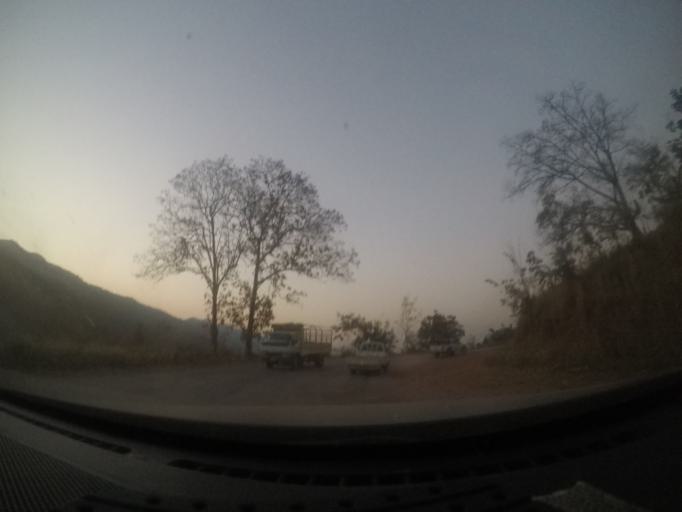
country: MM
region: Mandalay
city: Yamethin
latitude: 20.6941
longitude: 96.5041
